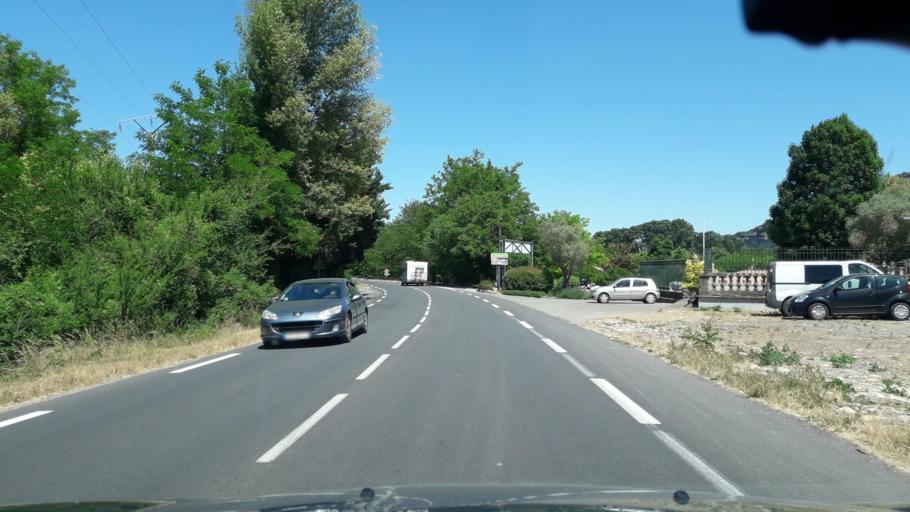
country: FR
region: Rhone-Alpes
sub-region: Departement de l'Ardeche
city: Ruoms
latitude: 44.4228
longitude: 4.3207
